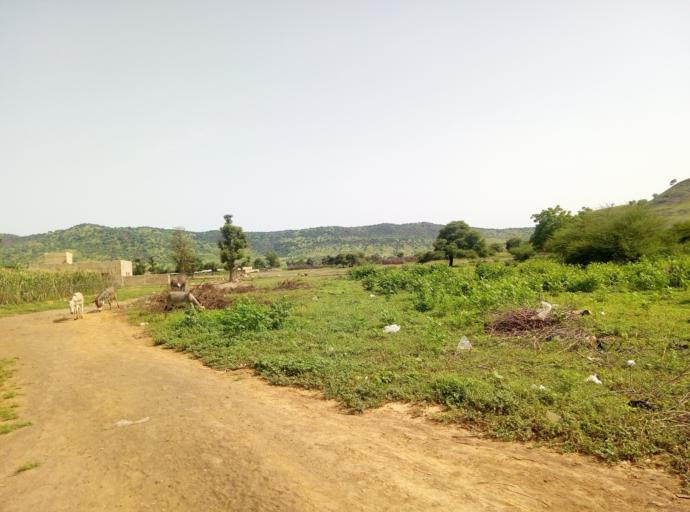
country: ML
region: Kayes
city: Yelimane
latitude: 14.6435
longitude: -10.6960
